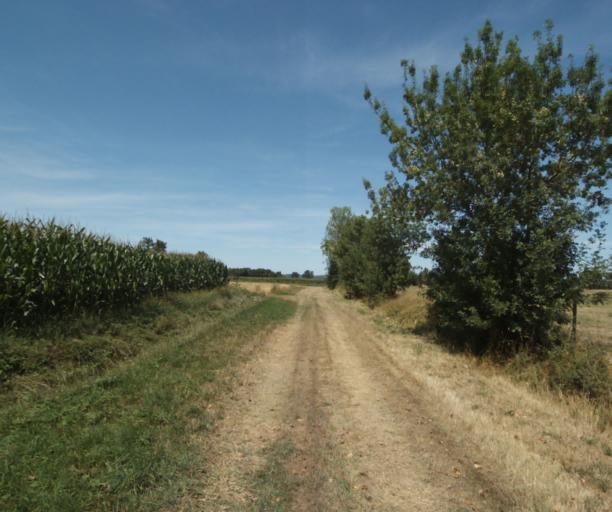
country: FR
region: Midi-Pyrenees
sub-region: Departement de la Haute-Garonne
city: Revel
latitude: 43.5033
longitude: 2.0295
